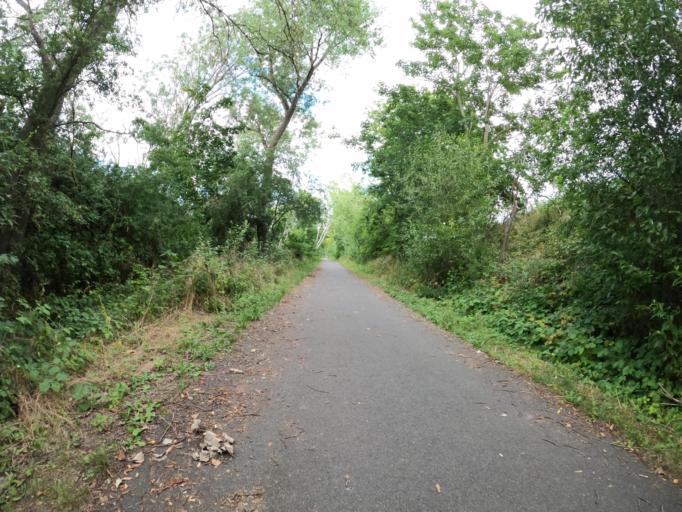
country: DE
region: Mecklenburg-Vorpommern
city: Woldegk
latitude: 53.3791
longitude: 13.5885
